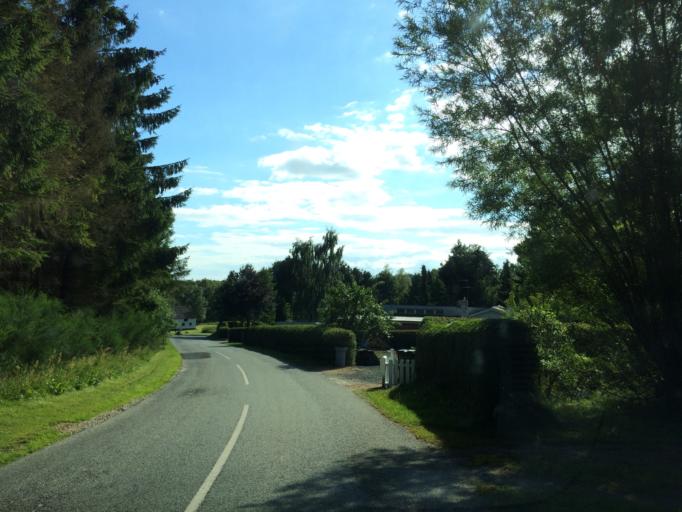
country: DK
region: Central Jutland
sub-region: Syddjurs Kommune
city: Ebeltoft
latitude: 56.2471
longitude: 10.6234
